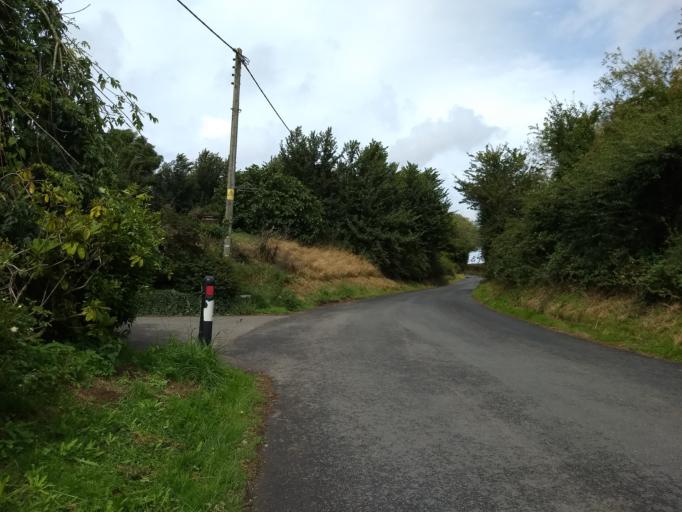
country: GB
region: England
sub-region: Isle of Wight
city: Newchurch
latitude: 50.6503
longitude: -1.2249
